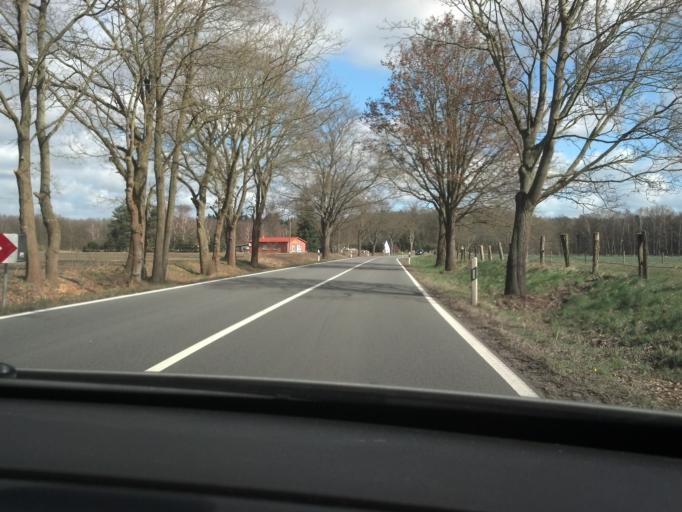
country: DE
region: Mecklenburg-Vorpommern
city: Boizenburg
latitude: 53.4365
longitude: 10.7506
